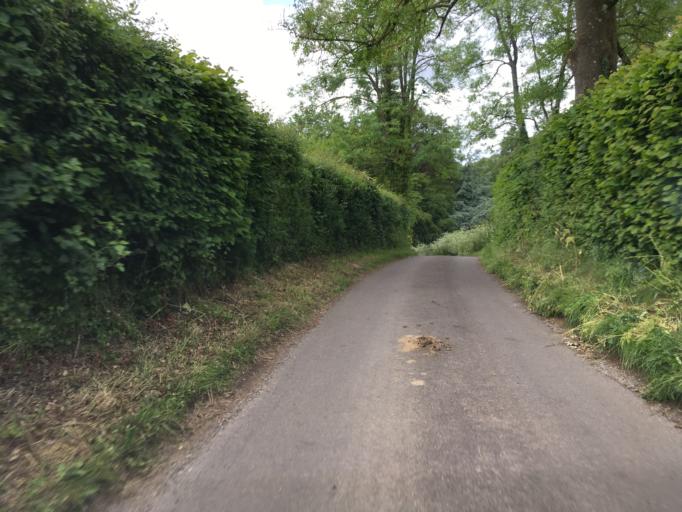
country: GB
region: England
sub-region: Gloucestershire
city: Cirencester
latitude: 51.7577
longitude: -1.9838
